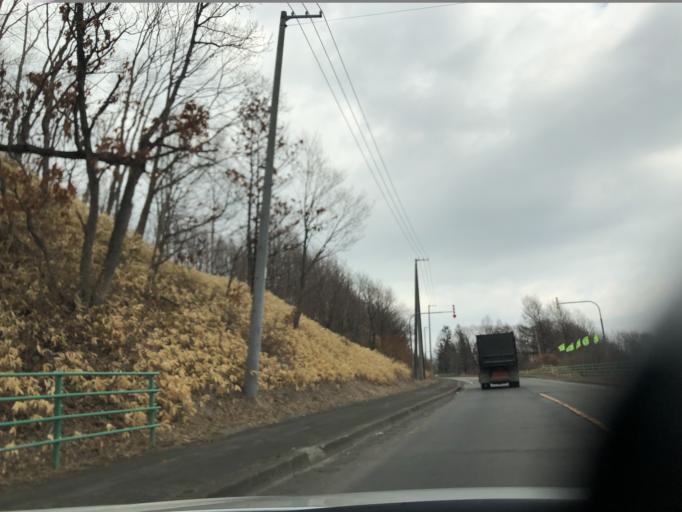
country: JP
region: Hokkaido
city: Chitose
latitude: 42.7595
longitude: 141.7988
